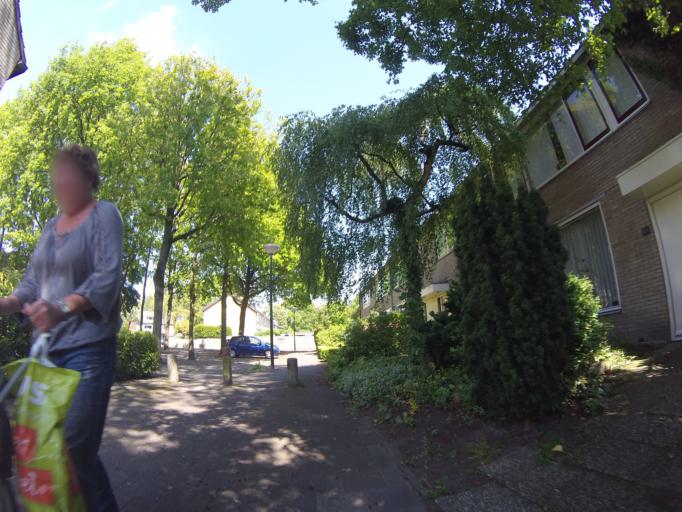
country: NL
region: Utrecht
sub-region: Gemeente Soest
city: Soest
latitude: 52.1741
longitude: 5.2823
